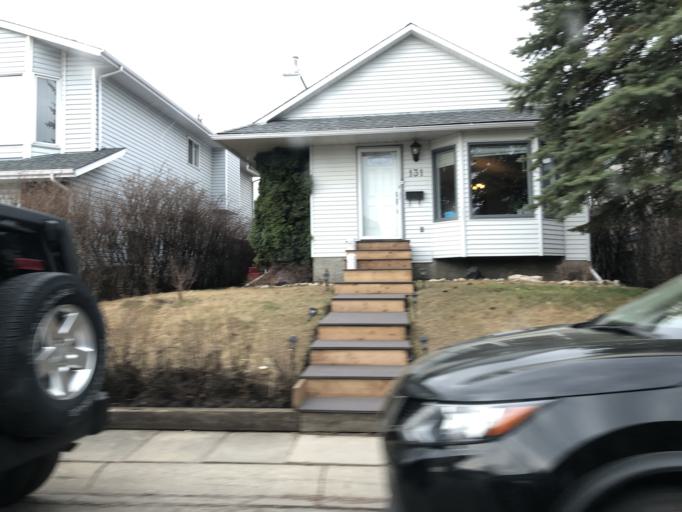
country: CA
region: Alberta
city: Calgary
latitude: 51.0735
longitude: -114.0118
